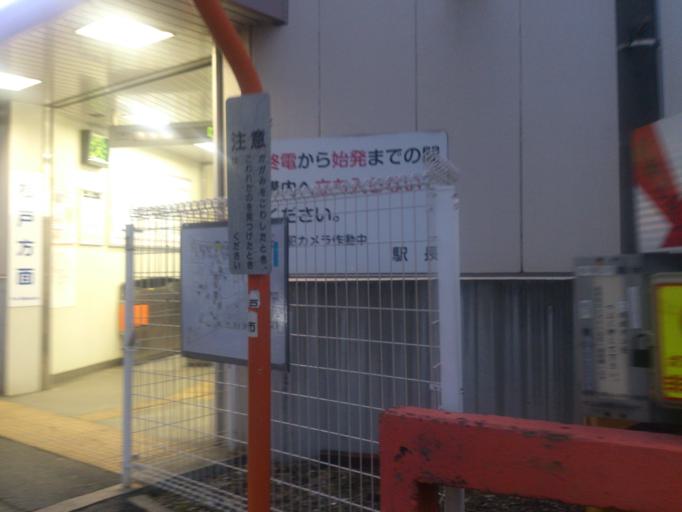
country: JP
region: Chiba
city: Matsudo
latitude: 35.7906
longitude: 139.9230
